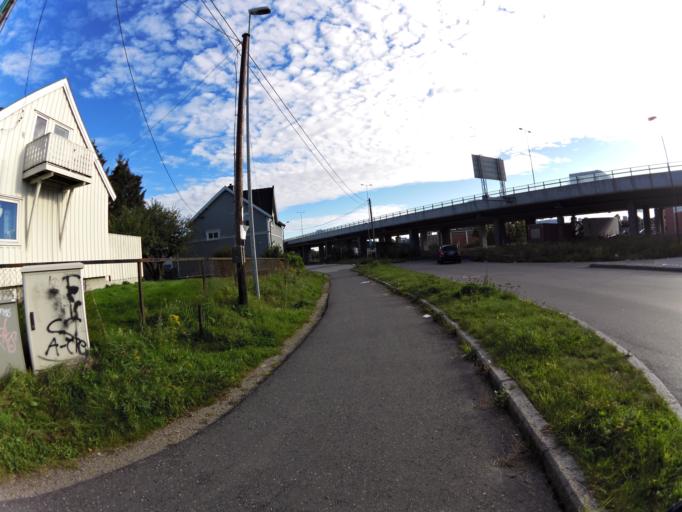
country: NO
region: Ostfold
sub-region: Sarpsborg
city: Sarpsborg
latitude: 59.2762
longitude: 11.0879
